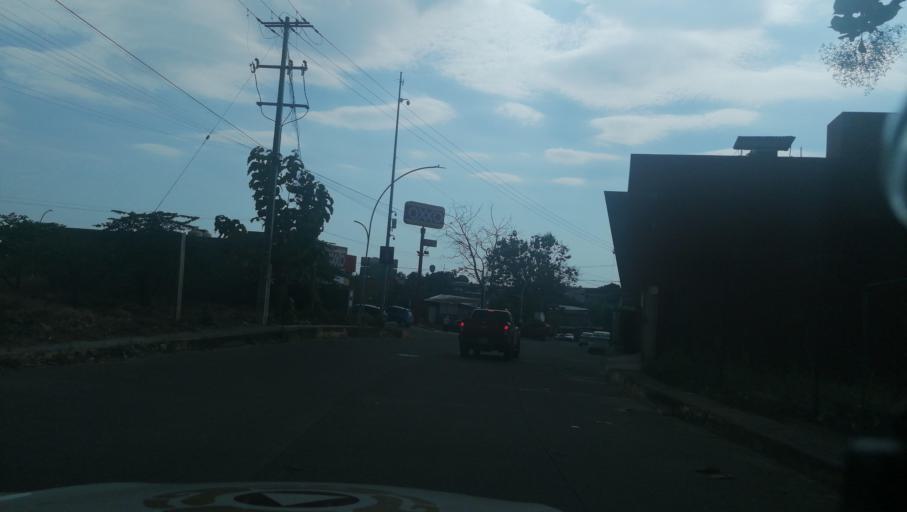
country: MX
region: Chiapas
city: Tapachula
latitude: 14.9286
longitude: -92.2520
